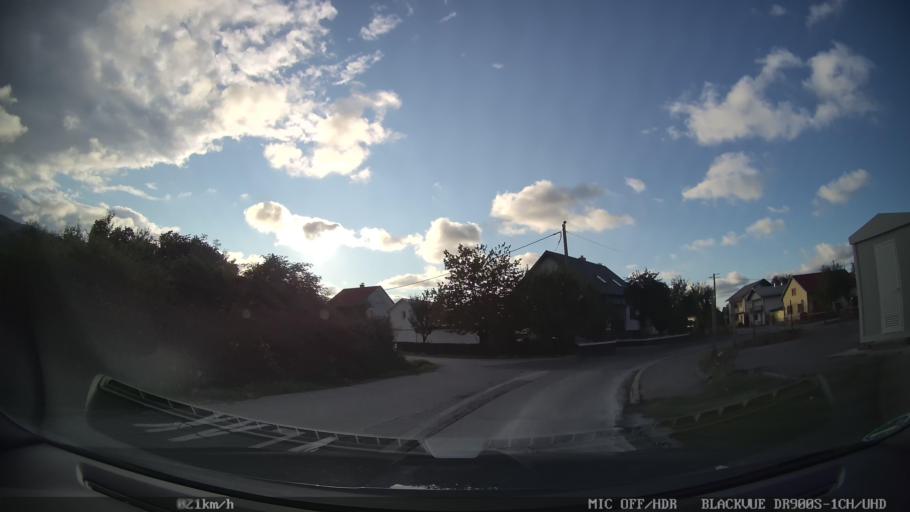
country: HR
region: Karlovacka
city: Plaski
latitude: 45.0762
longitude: 15.3672
